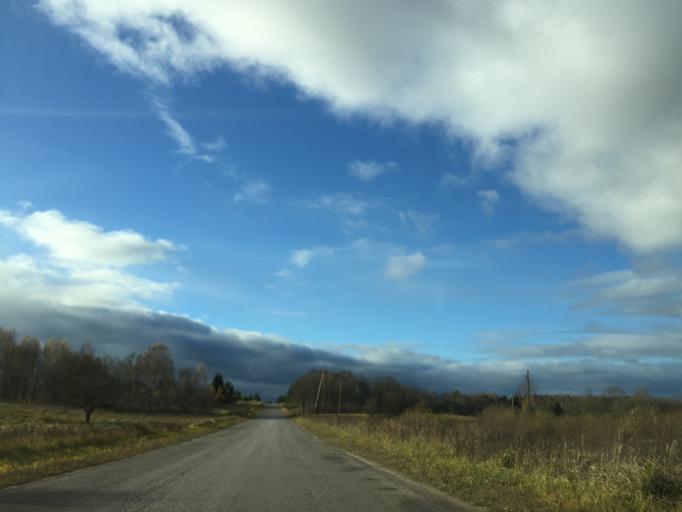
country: LV
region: Kandava
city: Kandava
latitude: 56.9682
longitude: 22.9570
